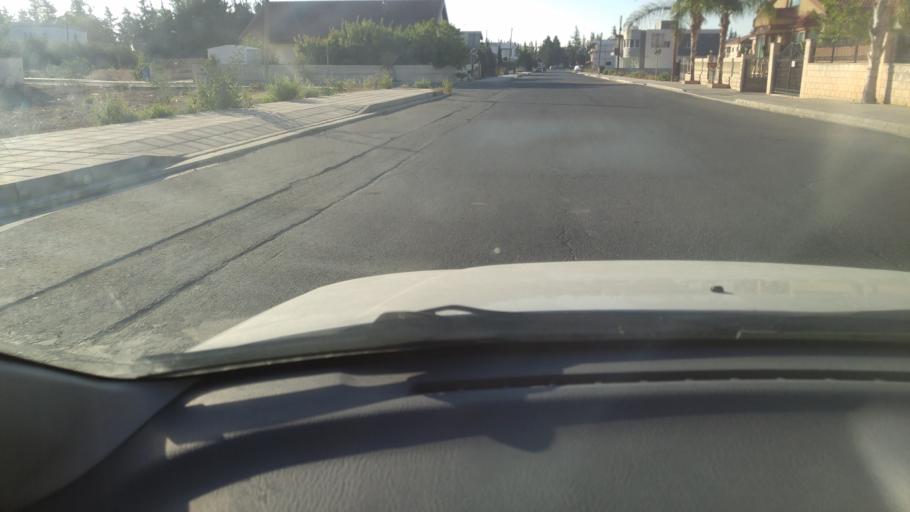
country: CY
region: Limassol
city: Ypsonas
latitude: 34.6566
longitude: 32.9737
